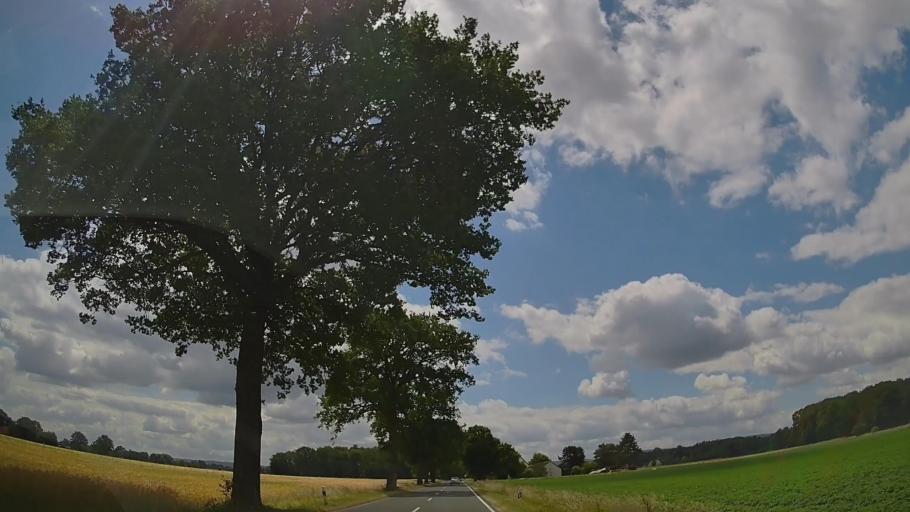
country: DE
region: North Rhine-Westphalia
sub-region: Regierungsbezirk Detmold
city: Hille
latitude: 52.3657
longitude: 8.7283
